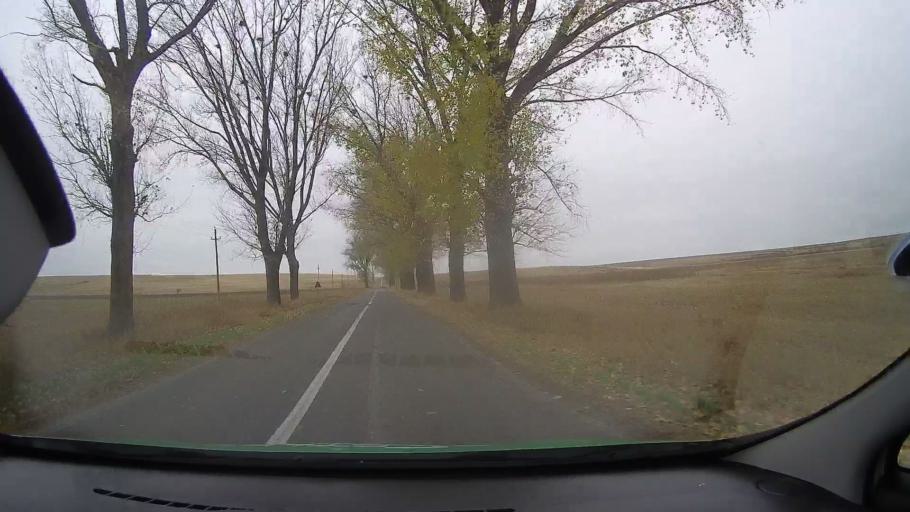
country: RO
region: Constanta
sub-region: Comuna Saraiu
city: Saraiu
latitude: 44.7268
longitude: 28.2197
